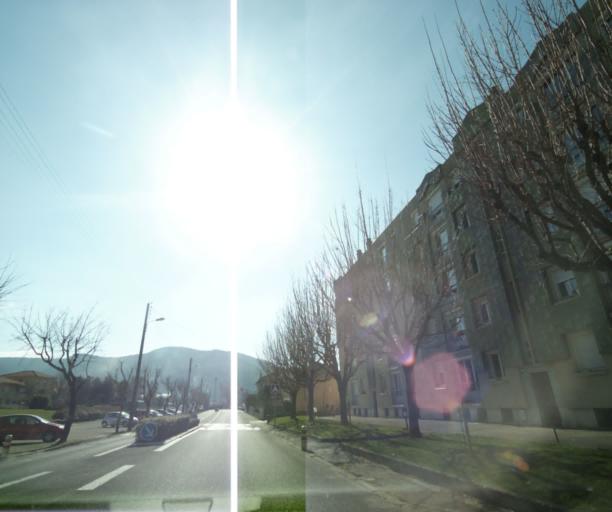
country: FR
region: Midi-Pyrenees
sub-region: Departement de l'Aveyron
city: Saint-Affrique
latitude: 43.9538
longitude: 2.8912
